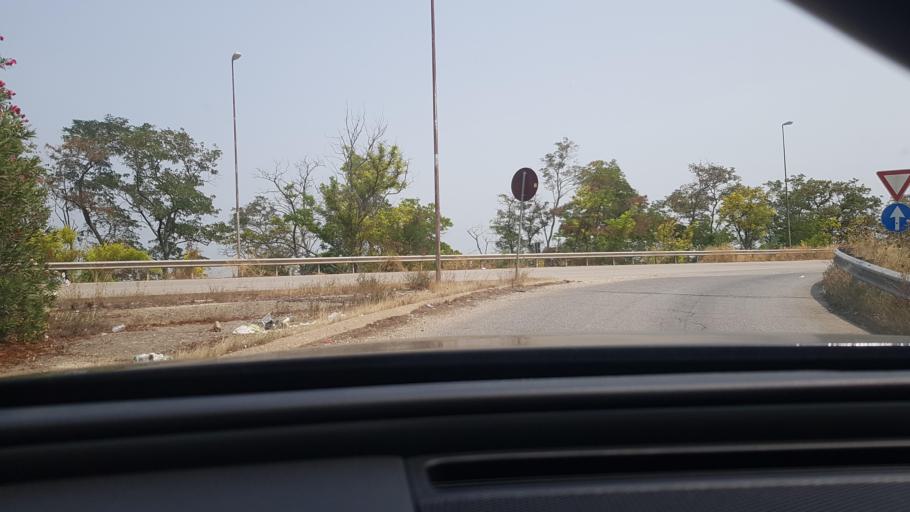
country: IT
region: Apulia
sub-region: Provincia di Barletta - Andria - Trani
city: Andria
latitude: 41.2148
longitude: 16.2664
